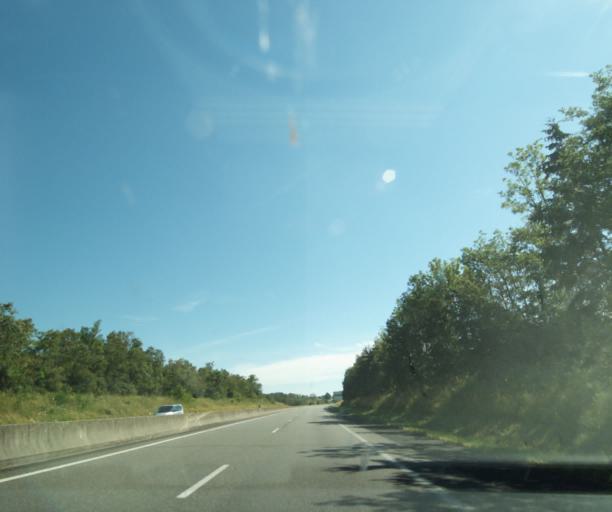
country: FR
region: Lorraine
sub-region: Departement des Vosges
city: Bulgneville
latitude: 48.2128
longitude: 5.8202
